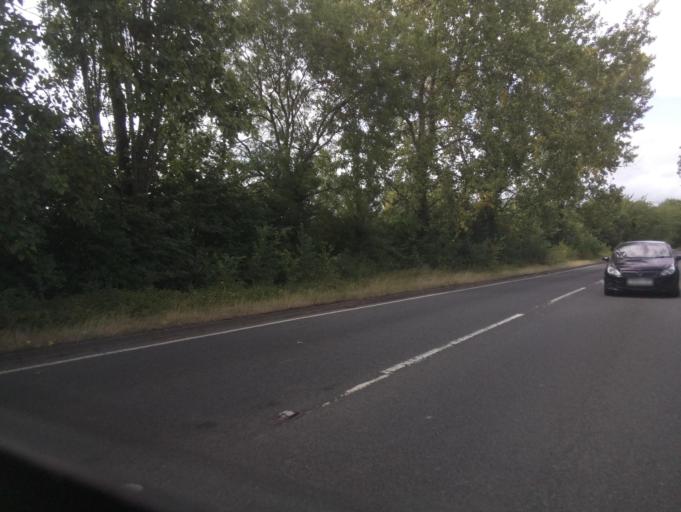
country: GB
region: England
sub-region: Warwickshire
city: Stratford-upon-Avon
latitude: 52.2261
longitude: -1.7390
